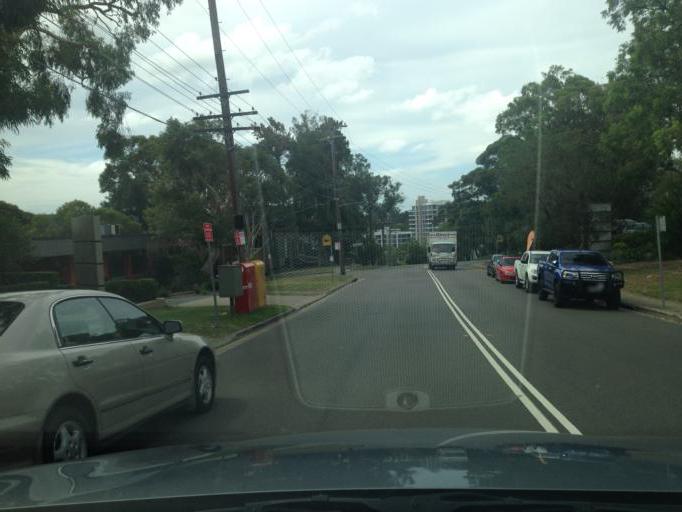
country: AU
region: New South Wales
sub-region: Lane Cove
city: Lane Cove West
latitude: -33.8095
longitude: 151.1463
